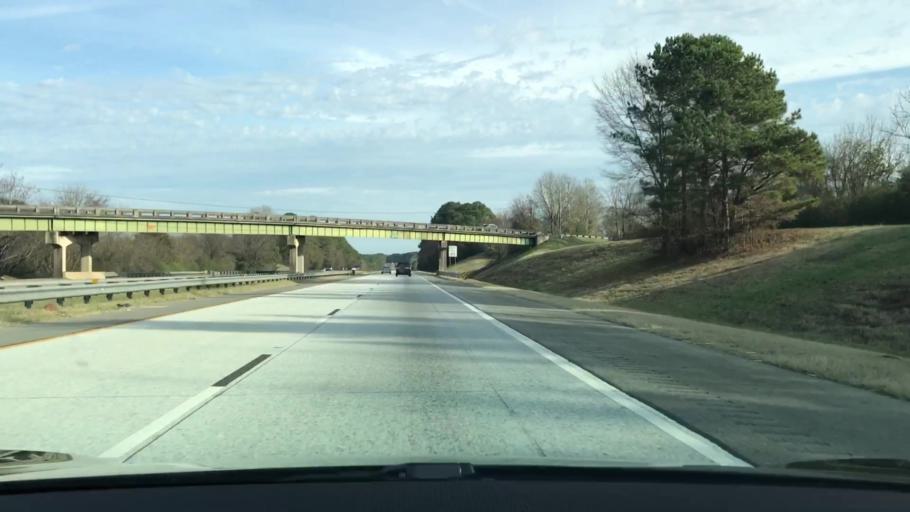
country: US
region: Georgia
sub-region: Putnam County
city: Jefferson
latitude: 33.5401
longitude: -83.3162
